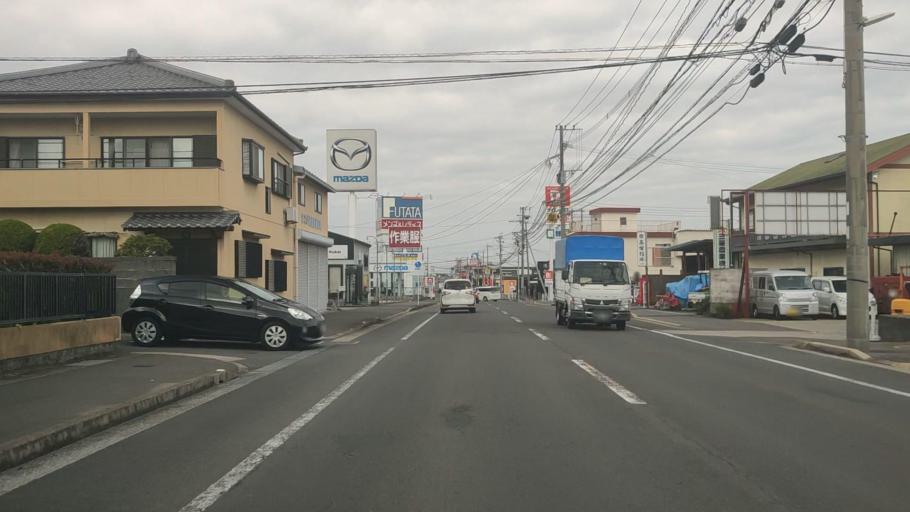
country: JP
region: Nagasaki
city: Shimabara
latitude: 32.8016
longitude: 130.3641
